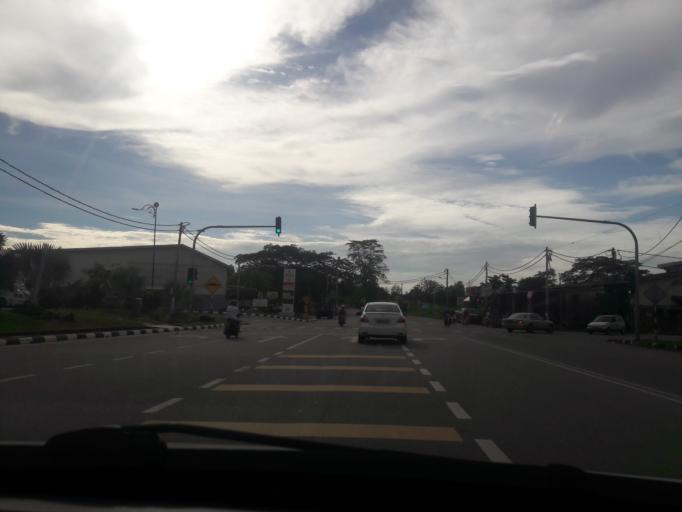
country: MY
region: Kedah
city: Sungai Petani
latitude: 5.6350
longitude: 100.5144
